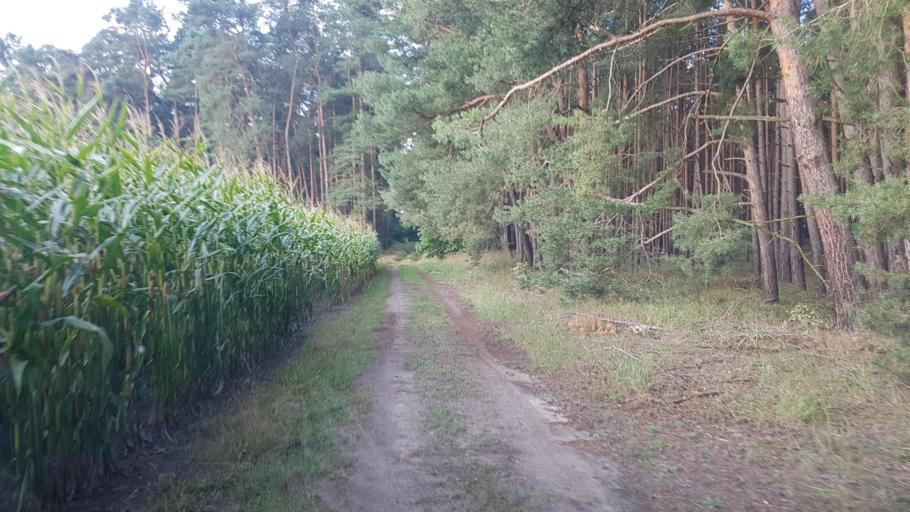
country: DE
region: Brandenburg
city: Schonewalde
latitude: 51.7041
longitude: 13.5803
